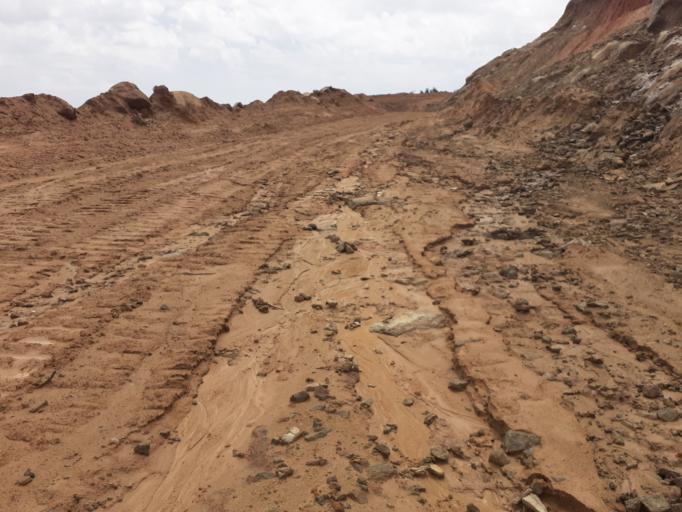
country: ET
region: Oromiya
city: Gimbi
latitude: 9.3322
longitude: 35.6931
